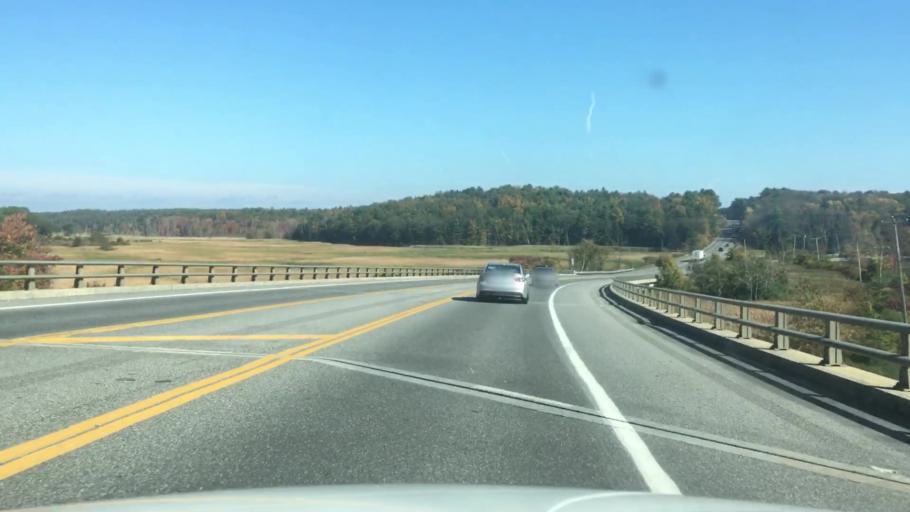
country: US
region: Maine
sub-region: Sagadahoc County
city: Woolwich
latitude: 43.9226
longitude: -69.7976
